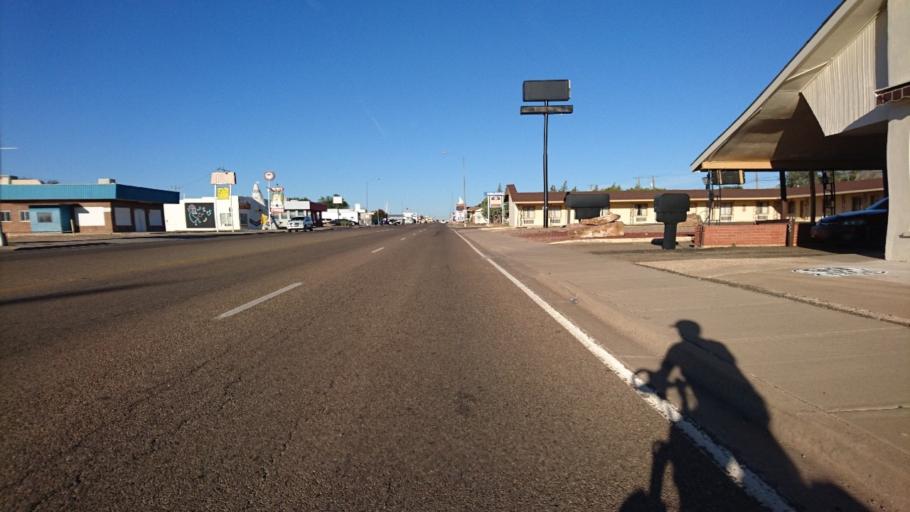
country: US
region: New Mexico
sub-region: Quay County
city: Tucumcari
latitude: 35.1719
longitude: -103.7138
